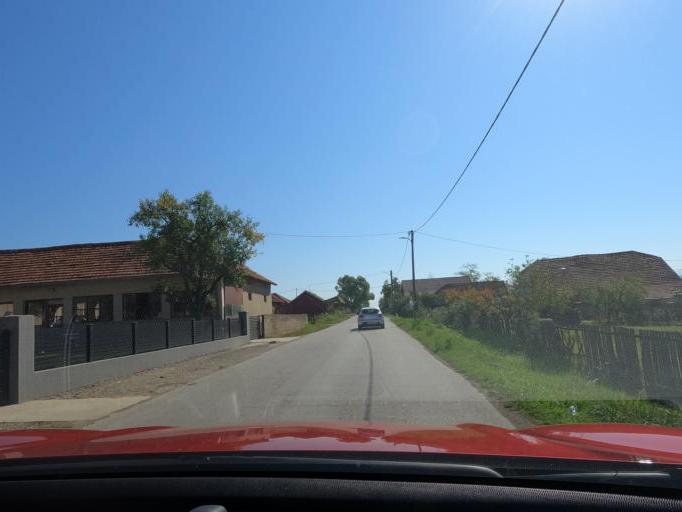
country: RS
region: Central Serbia
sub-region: Raski Okrug
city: Kraljevo
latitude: 43.7588
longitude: 20.6827
